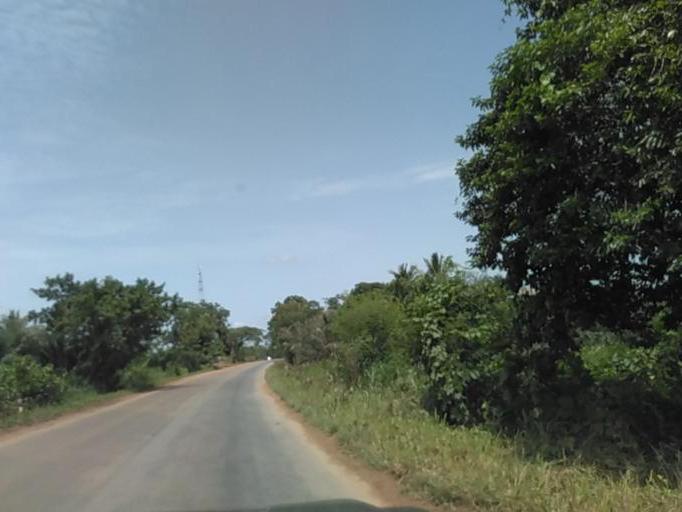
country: GH
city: Akropong
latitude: 6.1709
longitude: 0.0685
